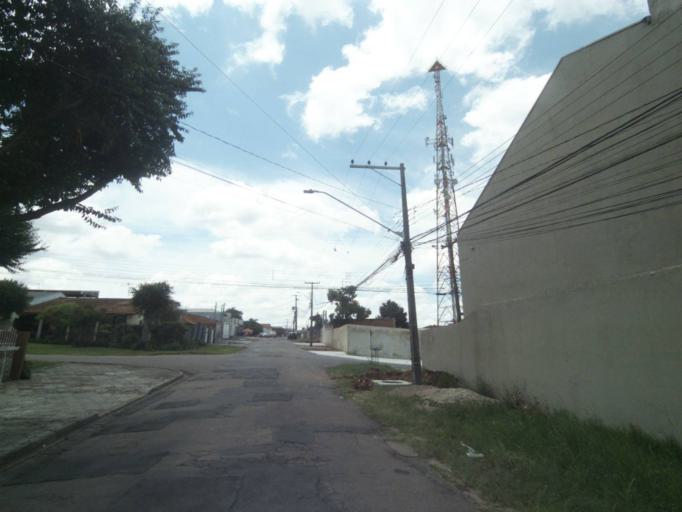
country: BR
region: Parana
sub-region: Curitiba
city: Curitiba
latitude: -25.4623
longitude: -49.3476
